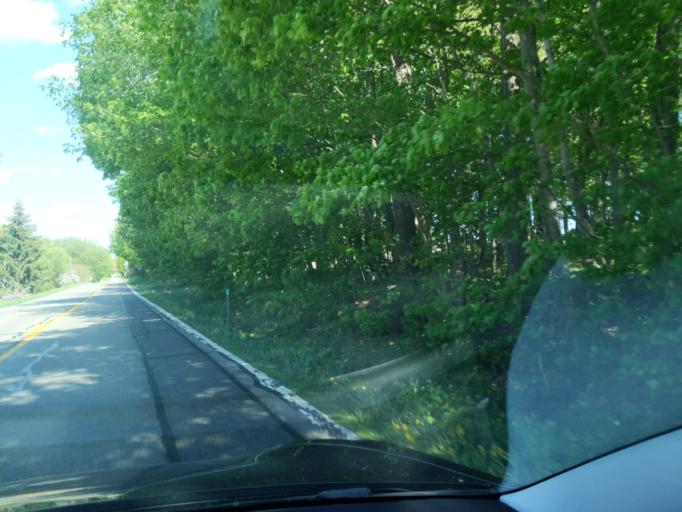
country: US
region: Michigan
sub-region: Kent County
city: Lowell
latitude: 42.7986
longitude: -85.3400
